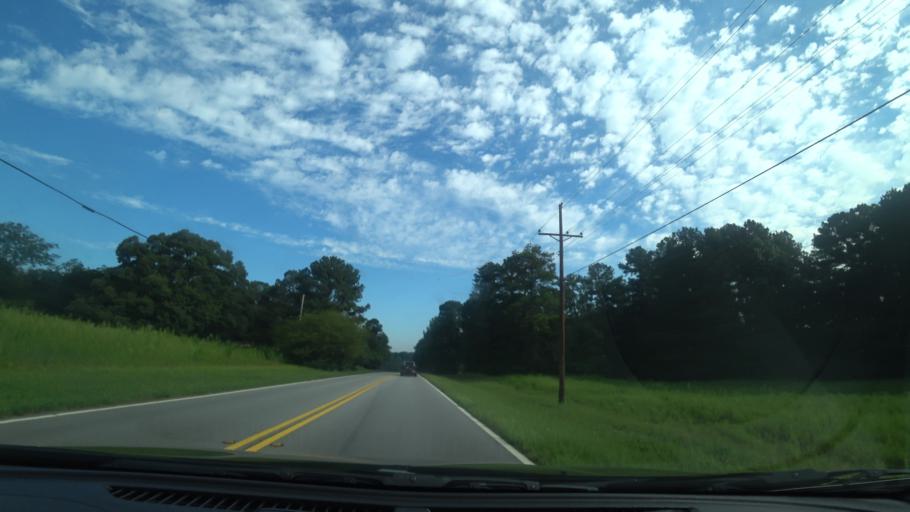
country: US
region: Georgia
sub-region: Rockdale County
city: Lakeview Estates
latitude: 33.7612
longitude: -83.9834
